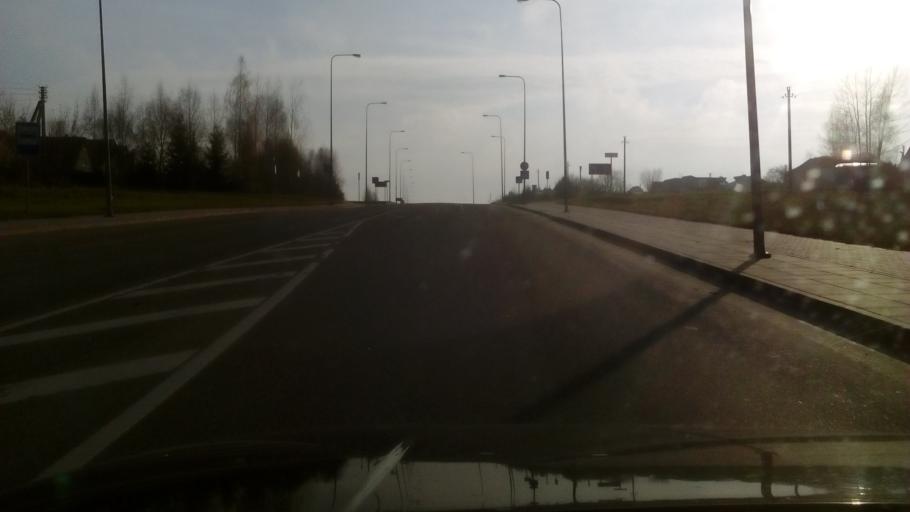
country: LT
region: Alytaus apskritis
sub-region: Alytus
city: Alytus
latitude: 54.3978
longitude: 23.9999
